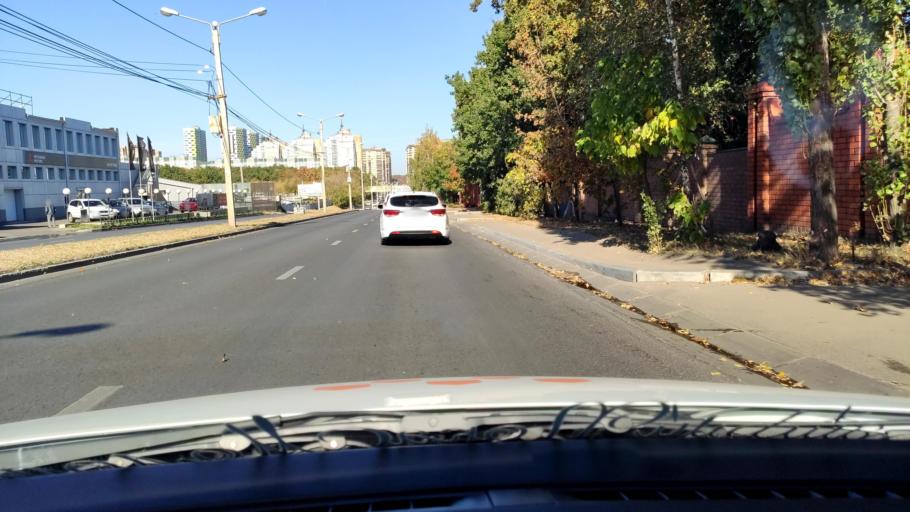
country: RU
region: Voronezj
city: Voronezh
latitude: 51.7055
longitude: 39.1958
